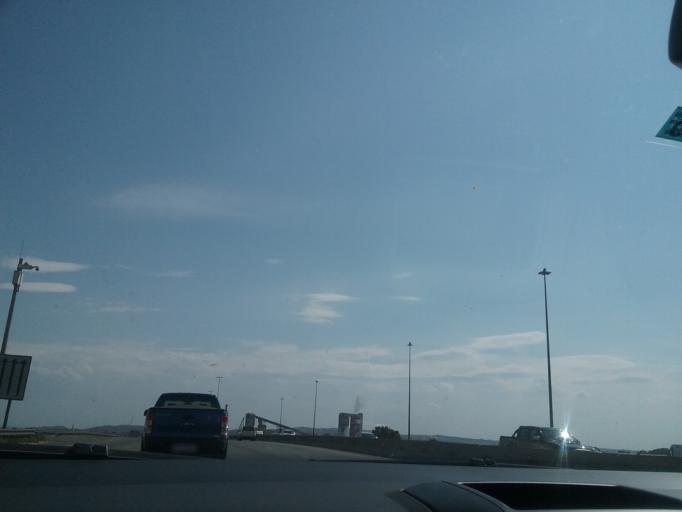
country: ZA
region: Gauteng
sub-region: Ekurhuleni Metropolitan Municipality
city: Germiston
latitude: -26.2146
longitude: 28.1330
